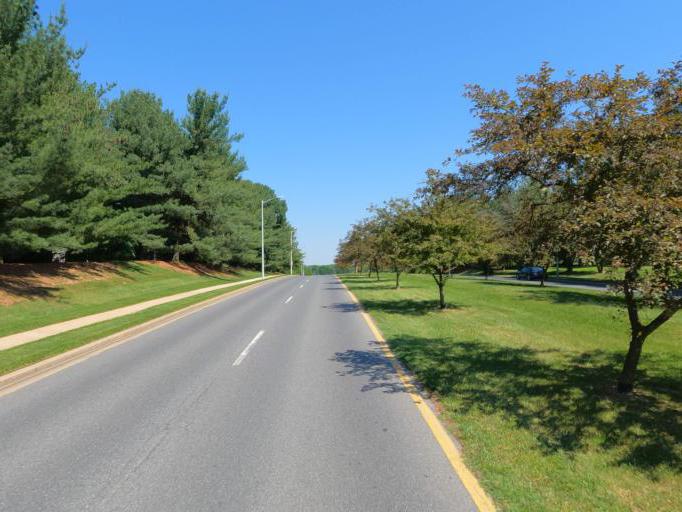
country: US
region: Maryland
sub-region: Montgomery County
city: Germantown
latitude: 39.1888
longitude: -77.2657
